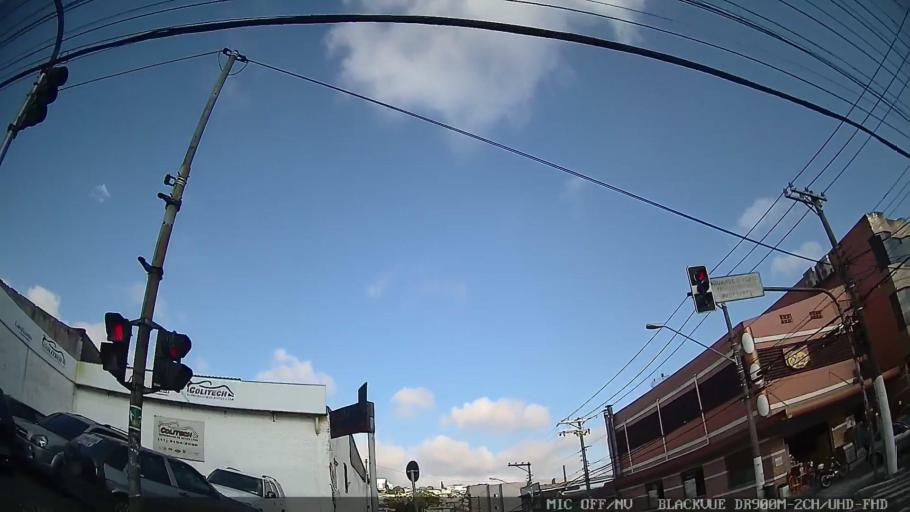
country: BR
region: Sao Paulo
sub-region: Sao Caetano Do Sul
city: Sao Caetano do Sul
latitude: -23.5731
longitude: -46.5409
